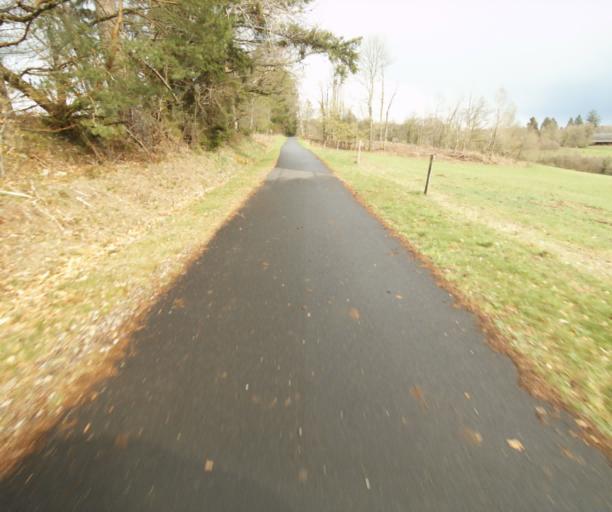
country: FR
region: Limousin
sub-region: Departement de la Correze
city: Saint-Privat
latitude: 45.2317
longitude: 1.9981
